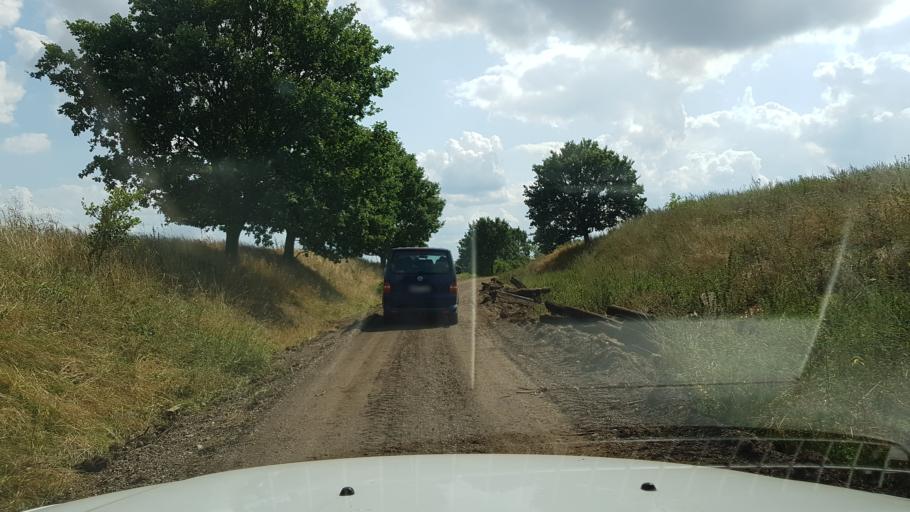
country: PL
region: West Pomeranian Voivodeship
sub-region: Powiat choszczenski
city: Pelczyce
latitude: 53.0752
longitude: 15.3104
